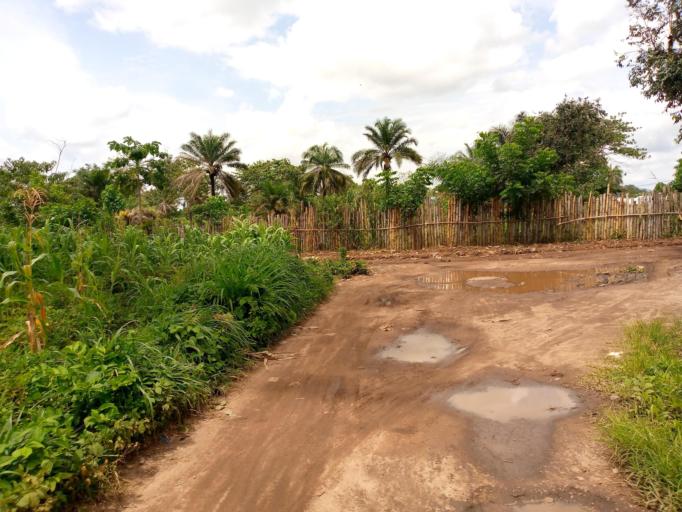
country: SL
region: Northern Province
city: Magburaka
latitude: 8.7234
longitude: -11.9326
